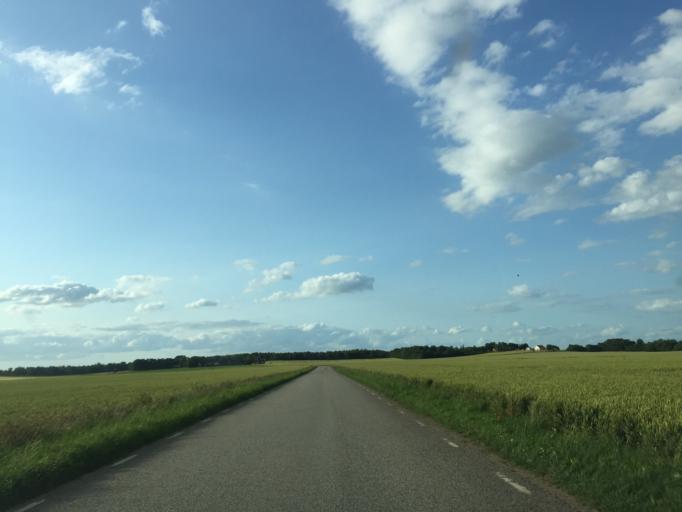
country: SE
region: OEstergoetland
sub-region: Vadstena Kommun
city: Vadstena
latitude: 58.4563
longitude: 14.8378
